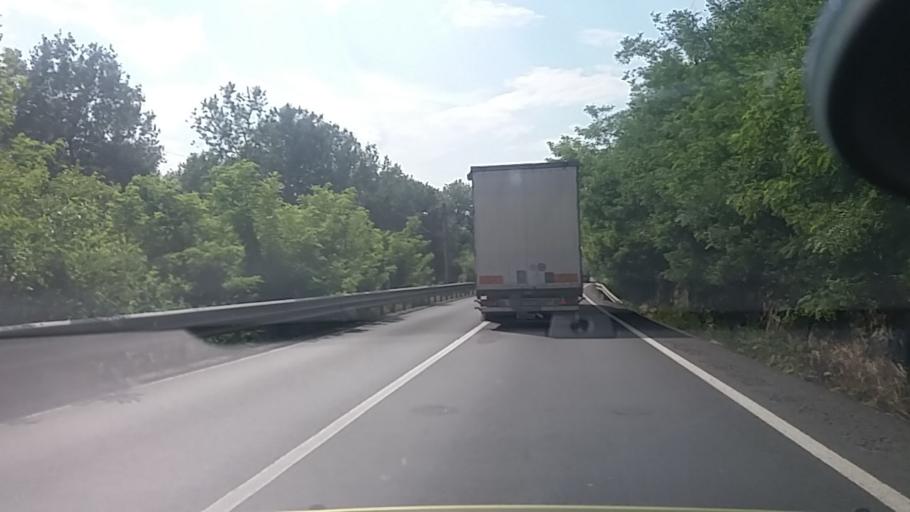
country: RO
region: Arad
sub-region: Comuna Savarsin
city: Savarsin
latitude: 46.0019
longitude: 22.2817
